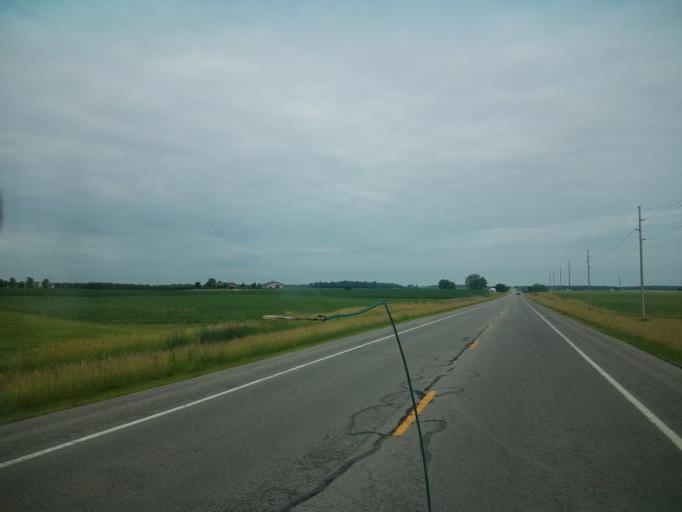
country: US
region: Ohio
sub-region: Hardin County
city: Kenton
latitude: 40.6638
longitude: -83.6501
